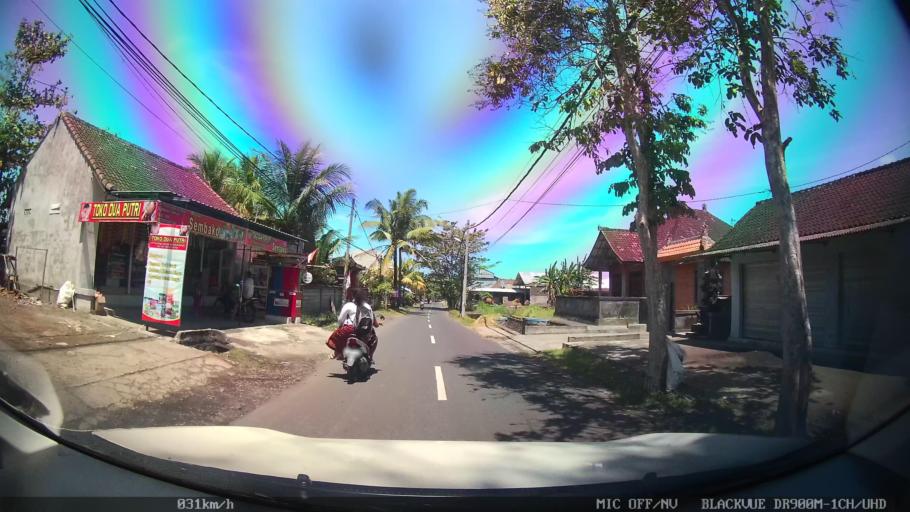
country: ID
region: Bali
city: Banjar Pasekan
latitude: -8.5698
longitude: 115.3217
